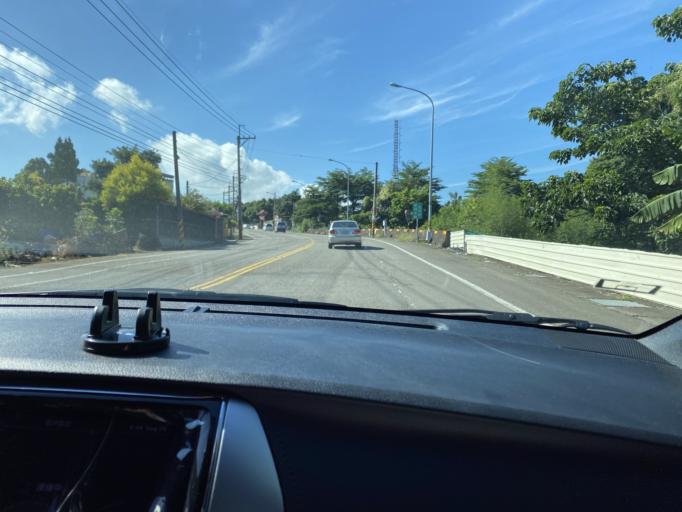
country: TW
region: Taiwan
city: Zhongxing New Village
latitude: 23.9689
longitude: 120.6243
